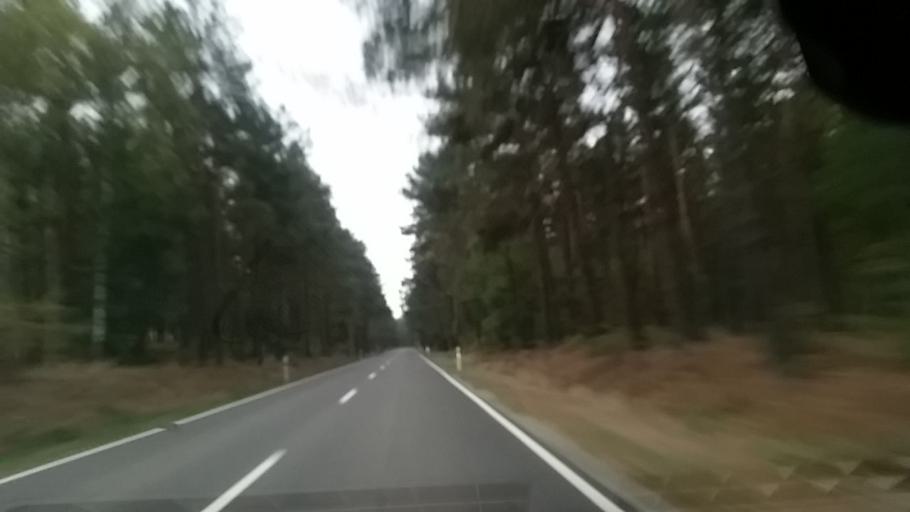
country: DE
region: Lower Saxony
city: Barwedel
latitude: 52.5846
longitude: 10.7899
